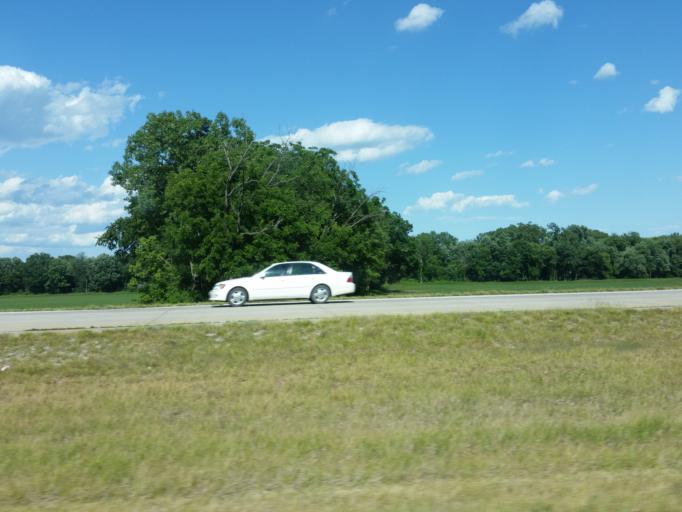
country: US
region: Missouri
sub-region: Lewis County
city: Canton
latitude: 40.2162
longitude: -91.5256
